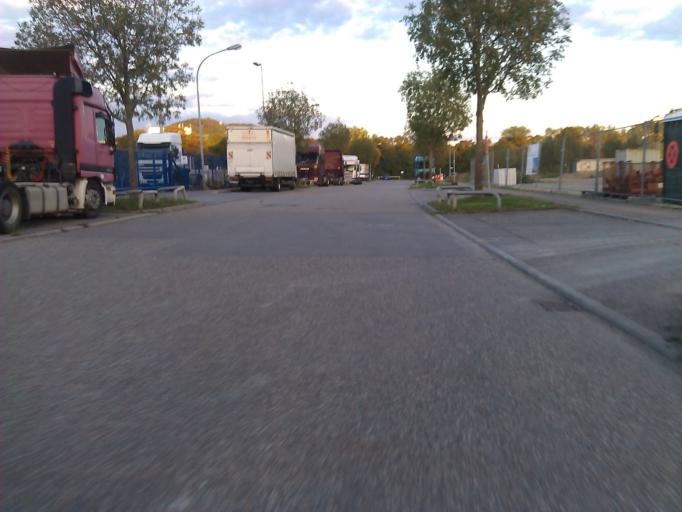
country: DE
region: Baden-Wuerttemberg
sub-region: Regierungsbezirk Stuttgart
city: Heilbronn
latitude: 49.1604
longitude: 9.2092
